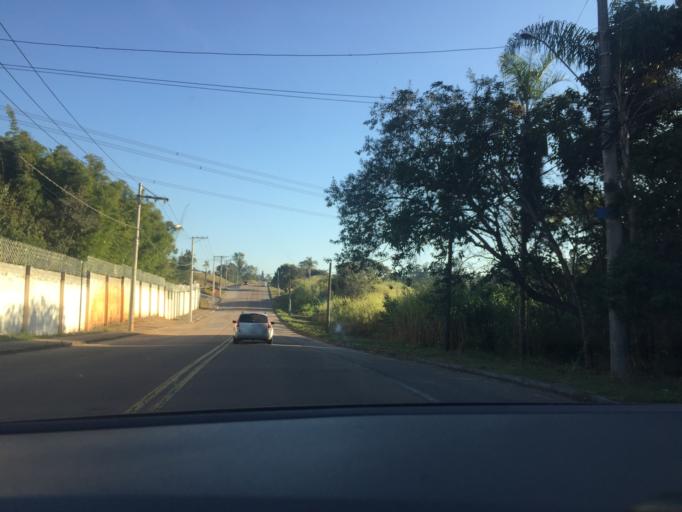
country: BR
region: Sao Paulo
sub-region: Louveira
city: Louveira
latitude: -23.1209
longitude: -46.9273
